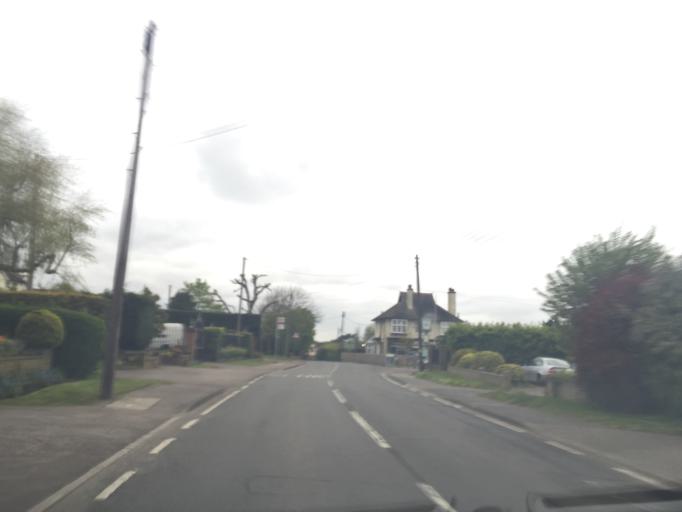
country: GB
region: England
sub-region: Greater London
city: Collier Row
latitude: 51.6279
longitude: 0.1840
